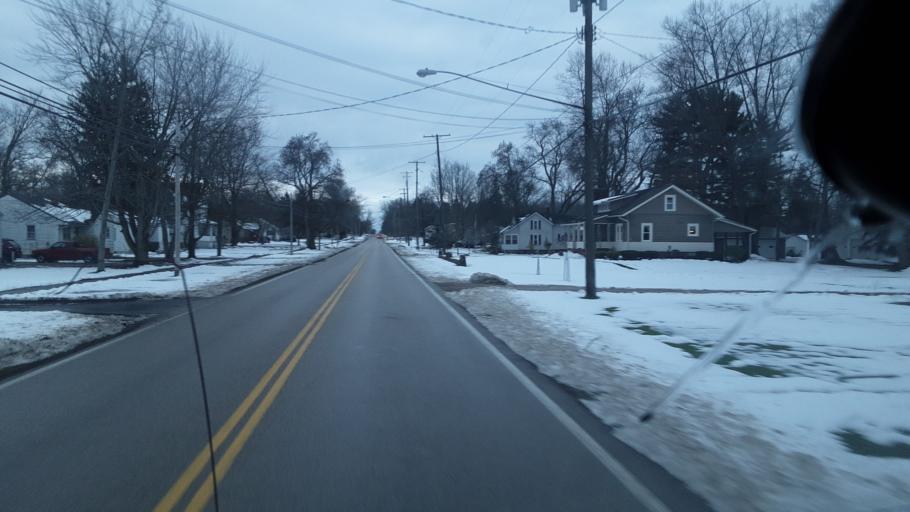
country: US
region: Ohio
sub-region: Ashtabula County
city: Jefferson
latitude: 41.7336
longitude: -80.7643
